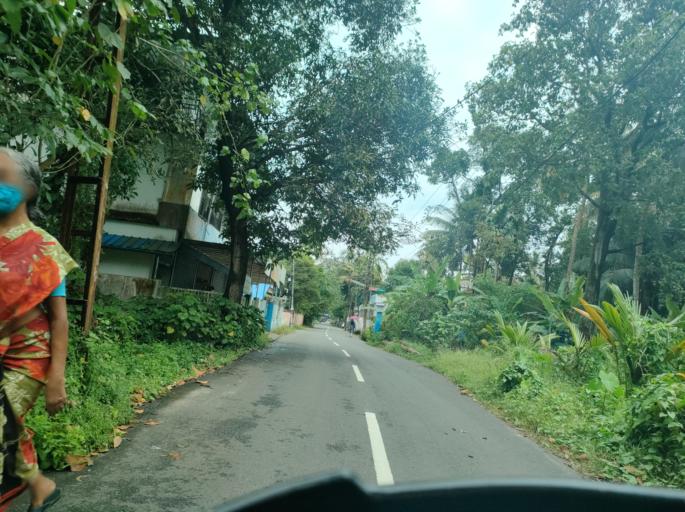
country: IN
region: Kerala
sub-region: Ernakulam
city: Elur
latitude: 10.0563
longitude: 76.2129
